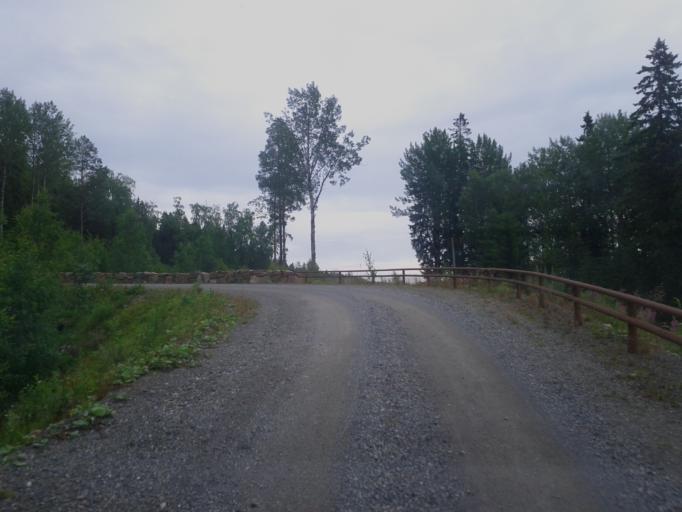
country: SE
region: Vaesternorrland
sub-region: OErnskoeldsviks Kommun
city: Bjasta
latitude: 63.0853
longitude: 18.4814
